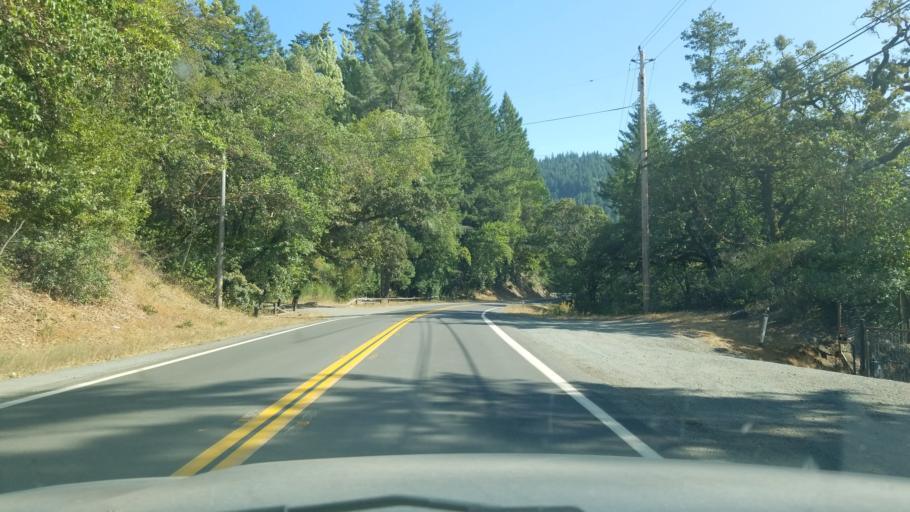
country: US
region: California
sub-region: Humboldt County
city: Redway
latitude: 40.2230
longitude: -123.8207
